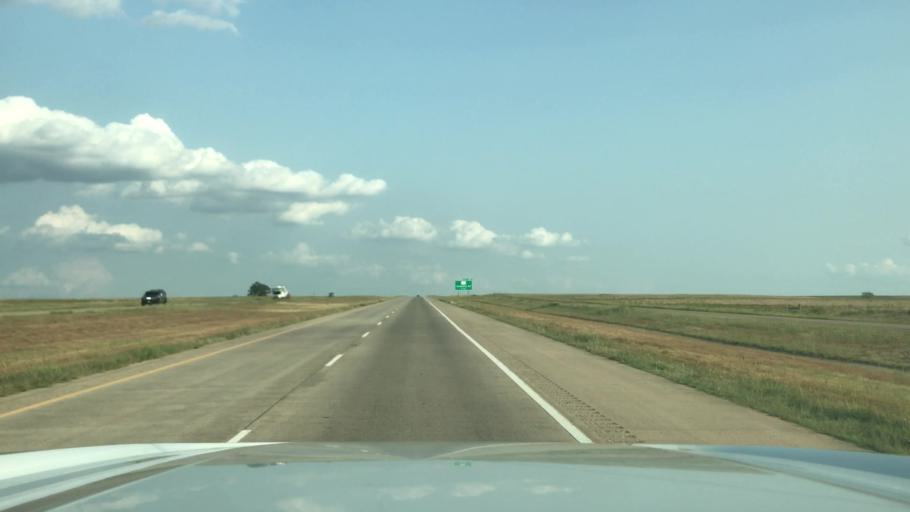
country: US
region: Texas
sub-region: Randall County
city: Canyon
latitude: 34.9605
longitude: -101.8635
